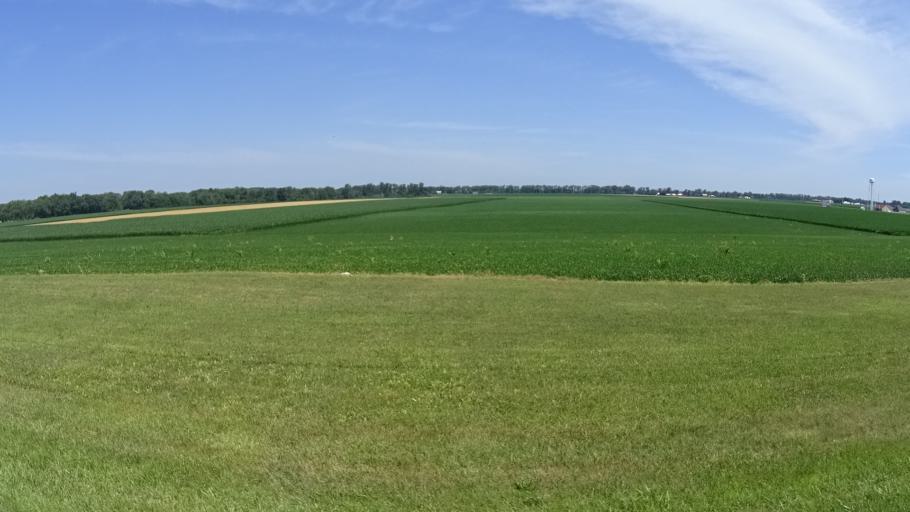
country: US
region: Ohio
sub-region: Erie County
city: Sandusky
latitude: 41.4040
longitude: -82.7938
